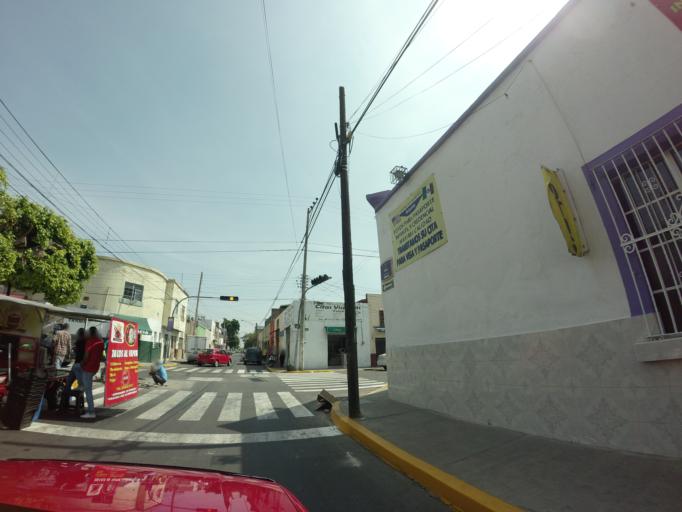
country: MX
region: Jalisco
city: Guadalajara
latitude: 20.6853
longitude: -103.3469
